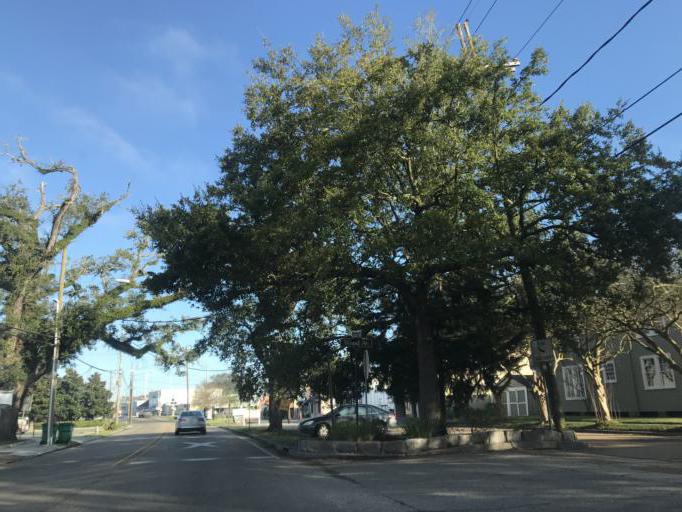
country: US
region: Louisiana
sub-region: Jefferson Parish
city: Metairie
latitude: 29.9854
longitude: -90.1292
